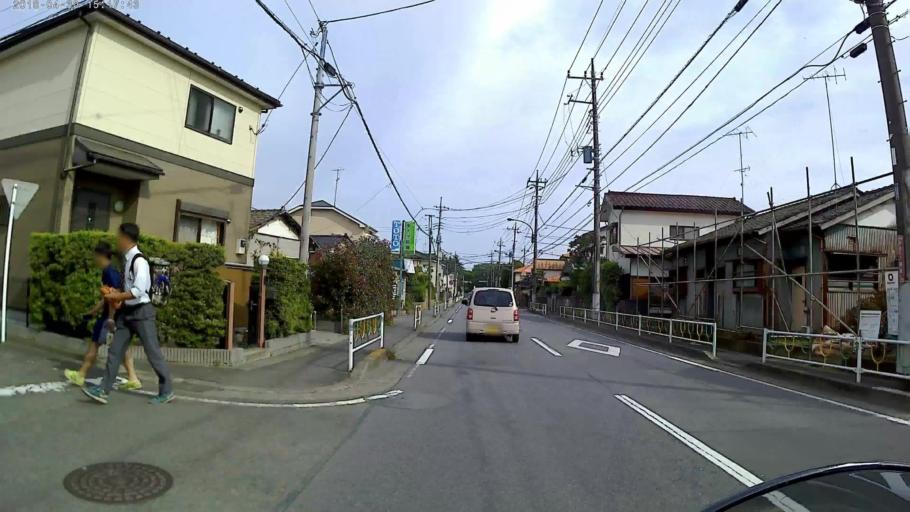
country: JP
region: Tokyo
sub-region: Machida-shi
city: Machida
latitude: 35.5613
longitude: 139.3887
